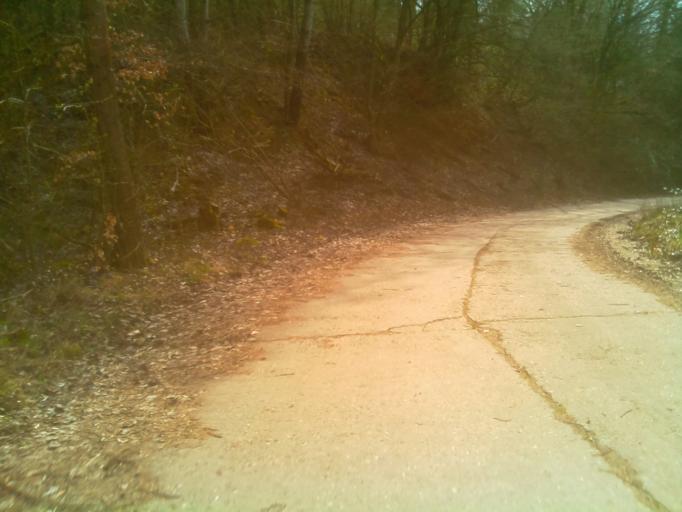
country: DE
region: Baden-Wuerttemberg
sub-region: Karlsruhe Region
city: Dossenheim
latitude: 49.4467
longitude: 8.6836
